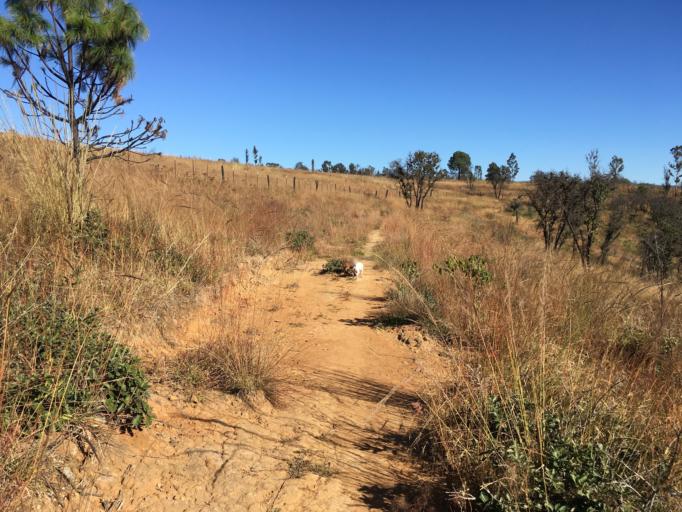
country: MX
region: Michoacan
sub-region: Morelia
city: Montana Monarca (Punta Altozano)
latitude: 19.6613
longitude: -101.1463
